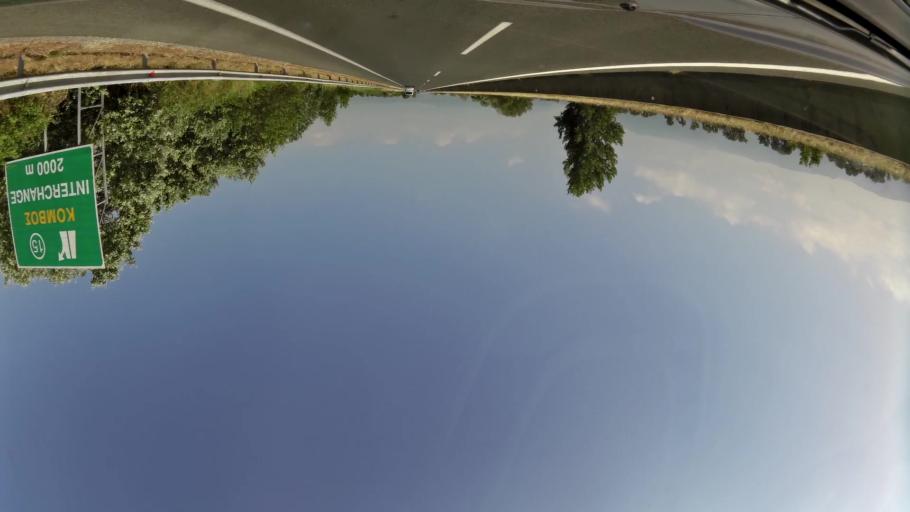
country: GR
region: Central Macedonia
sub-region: Nomos Imathias
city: Kouloura
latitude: 40.5514
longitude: 22.3379
